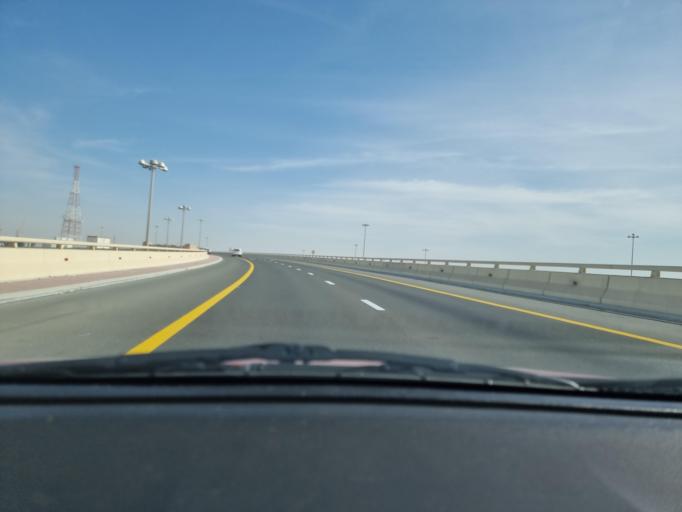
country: AE
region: Abu Dhabi
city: Abu Dhabi
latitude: 24.3102
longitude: 54.5998
